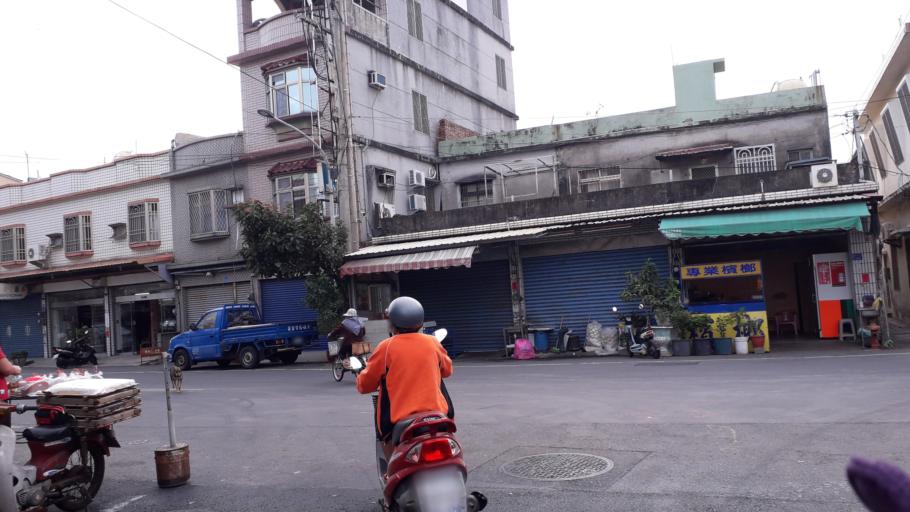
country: TW
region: Taiwan
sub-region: Pingtung
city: Pingtung
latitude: 22.3622
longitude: 120.5959
